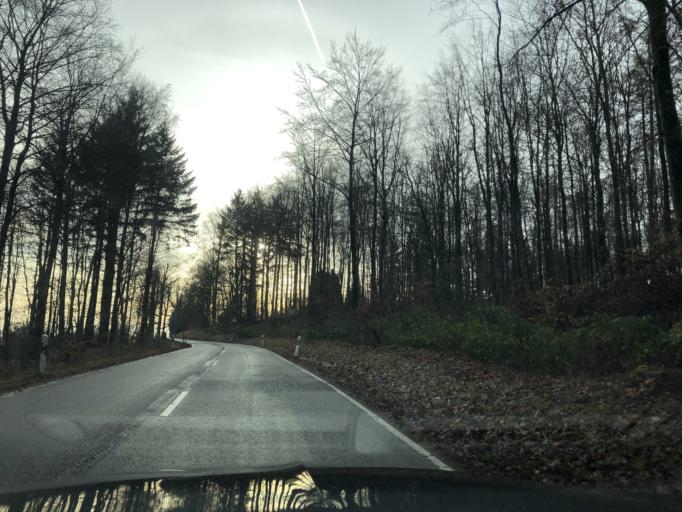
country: DE
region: Baden-Wuerttemberg
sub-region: Karlsruhe Region
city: Gaiberg
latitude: 49.3866
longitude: 8.7314
